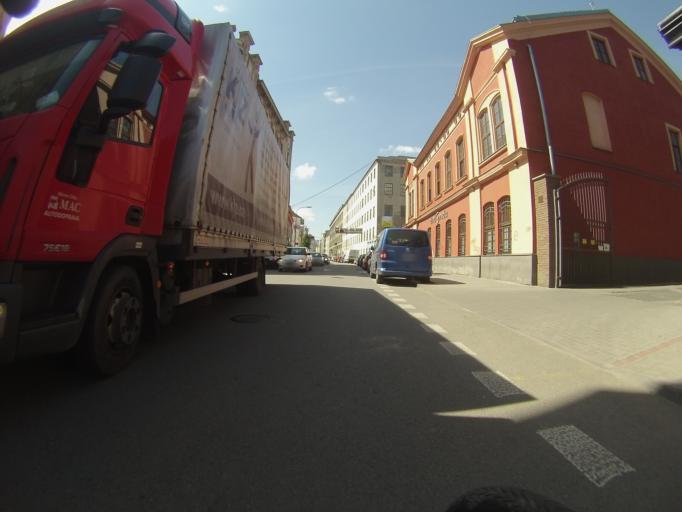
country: CZ
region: South Moravian
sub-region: Mesto Brno
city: Brno
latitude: 49.1940
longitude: 16.6221
